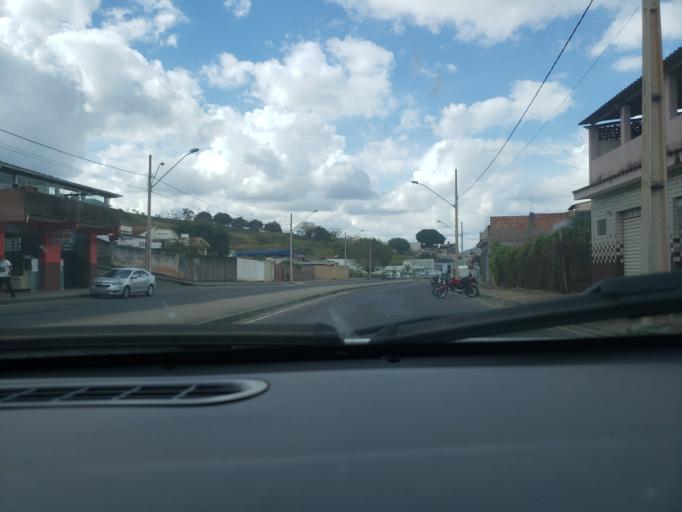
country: BR
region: Minas Gerais
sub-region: Campo Belo
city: Campo Belo
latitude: -20.9012
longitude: -45.2733
